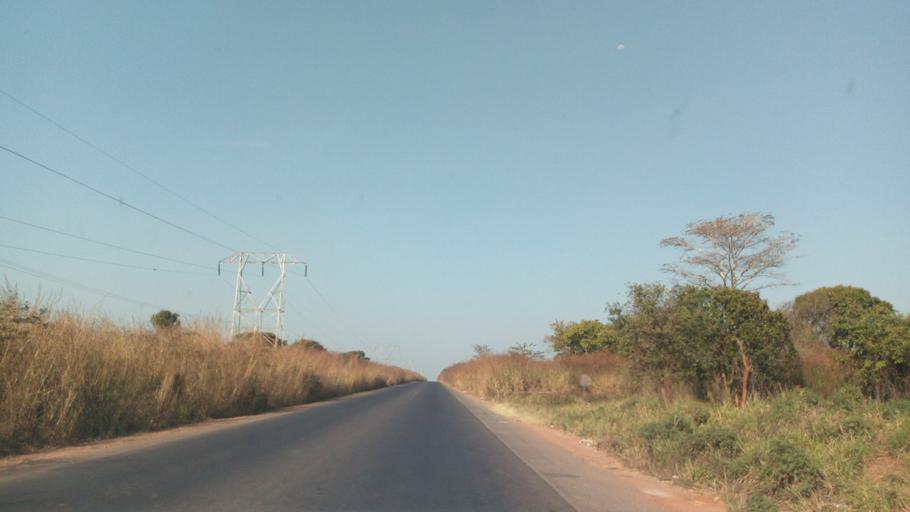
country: CD
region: Katanga
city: Likasi
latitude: -11.0016
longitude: 26.8678
